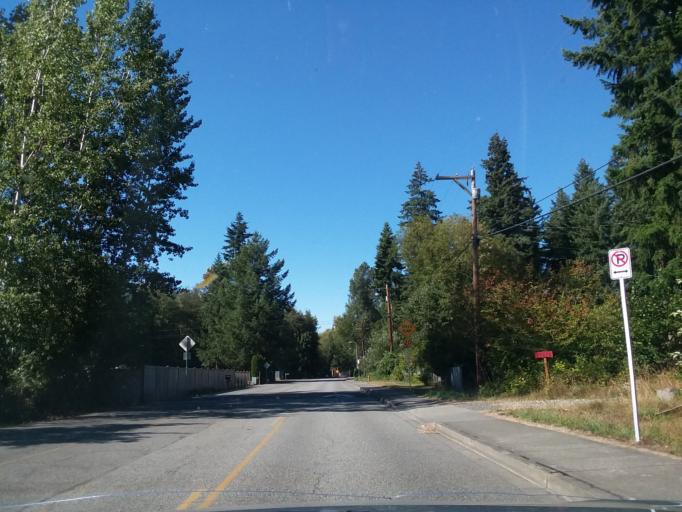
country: US
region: Washington
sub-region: Snohomish County
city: Smokey Point
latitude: 48.1583
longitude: -122.1966
